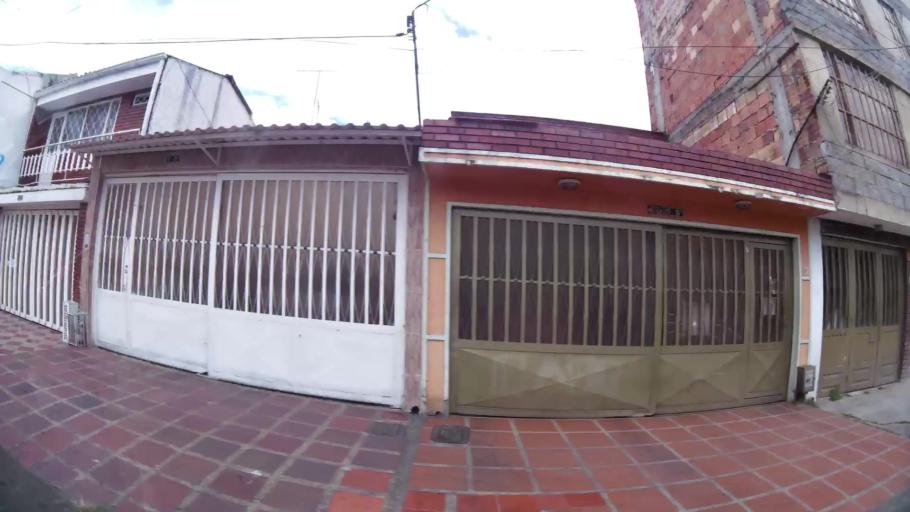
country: CO
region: Bogota D.C.
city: Bogota
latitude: 4.6095
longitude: -74.1217
